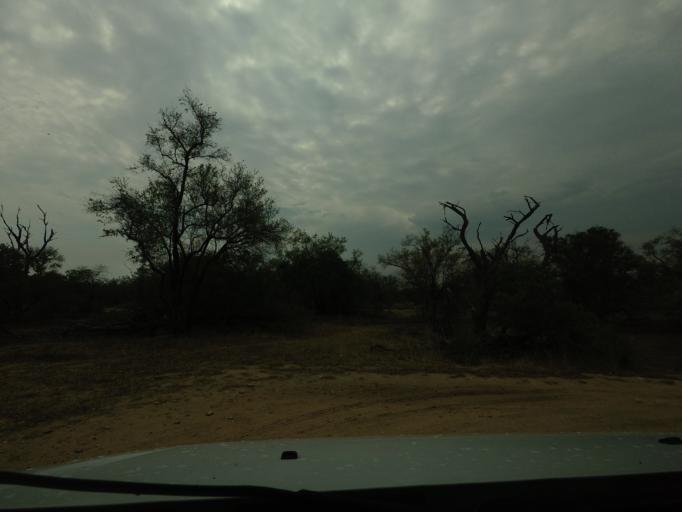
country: ZA
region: Limpopo
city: Thulamahashi
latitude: -24.4060
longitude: 31.5236
